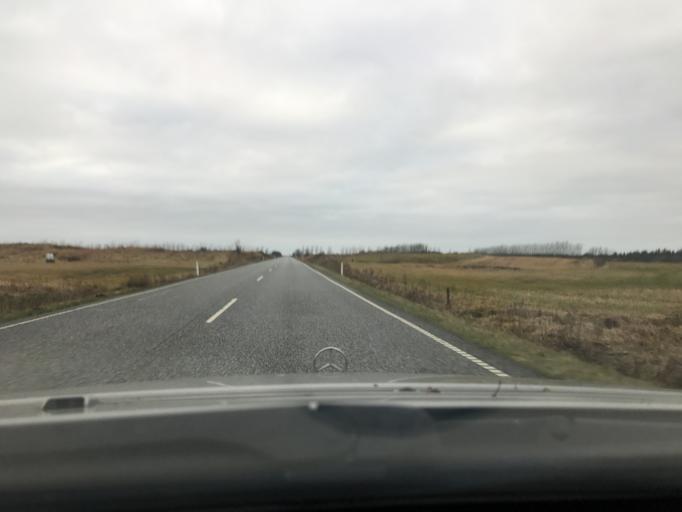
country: DK
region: South Denmark
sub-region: Tonder Kommune
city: Sherrebek
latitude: 55.1762
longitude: 8.8302
